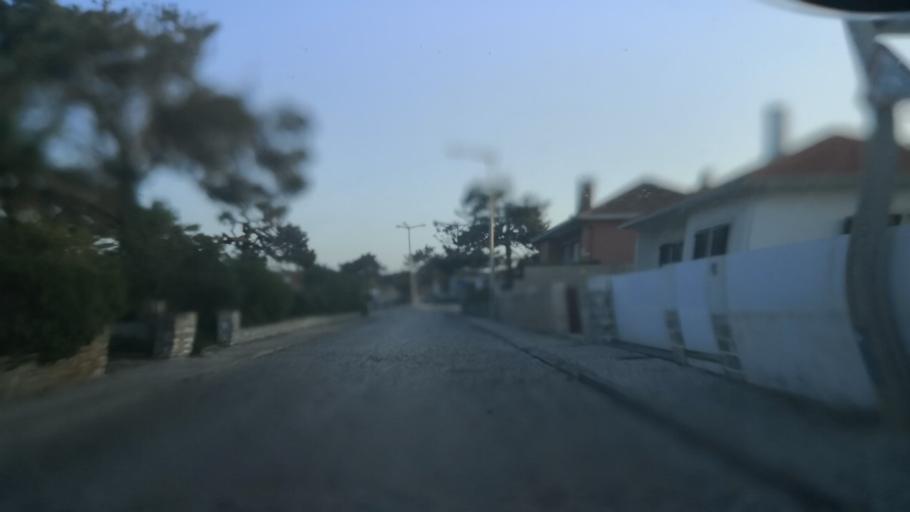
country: PT
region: Leiria
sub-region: Alcobaca
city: Pataias
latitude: 39.7586
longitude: -9.0299
